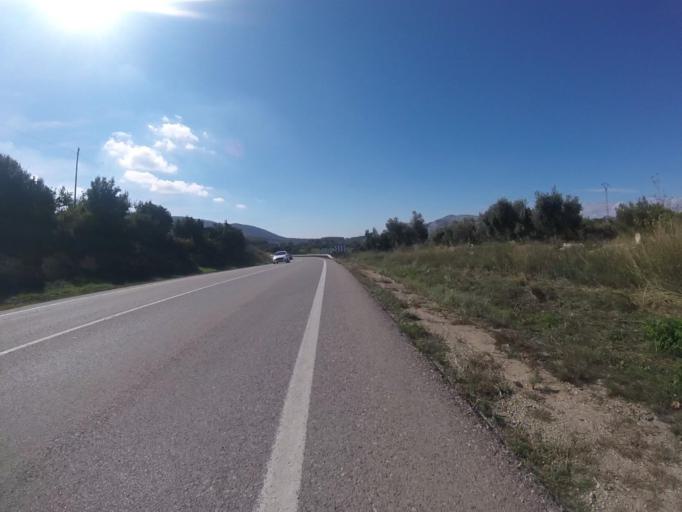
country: ES
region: Valencia
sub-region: Provincia de Castello
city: Albocasser
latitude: 40.3356
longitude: -0.0125
